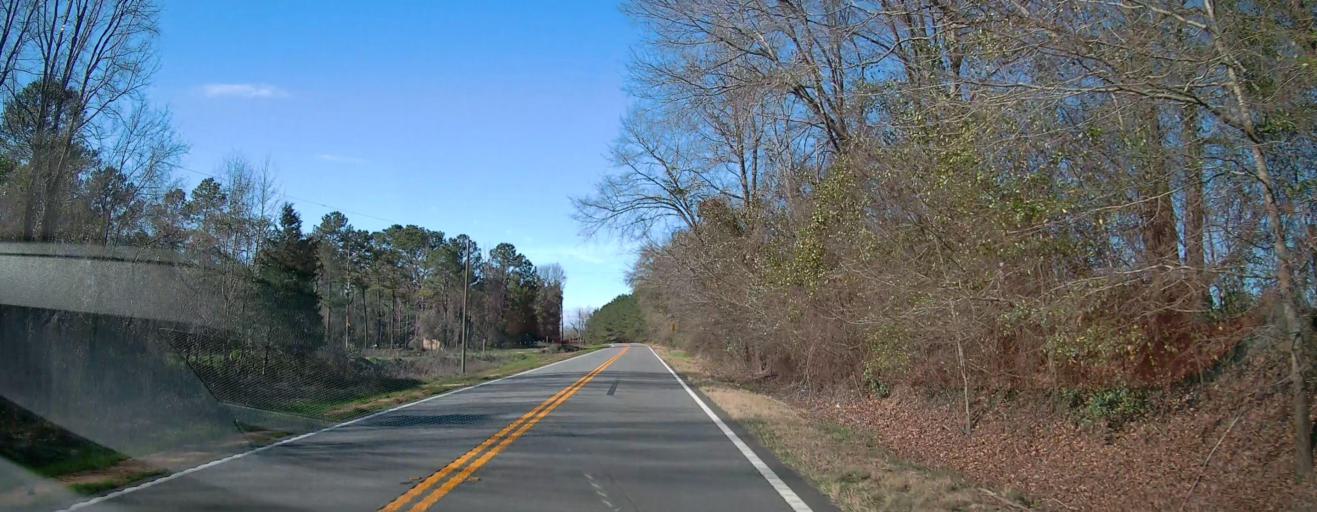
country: US
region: Georgia
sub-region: Macon County
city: Oglethorpe
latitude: 32.3819
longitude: -84.1910
